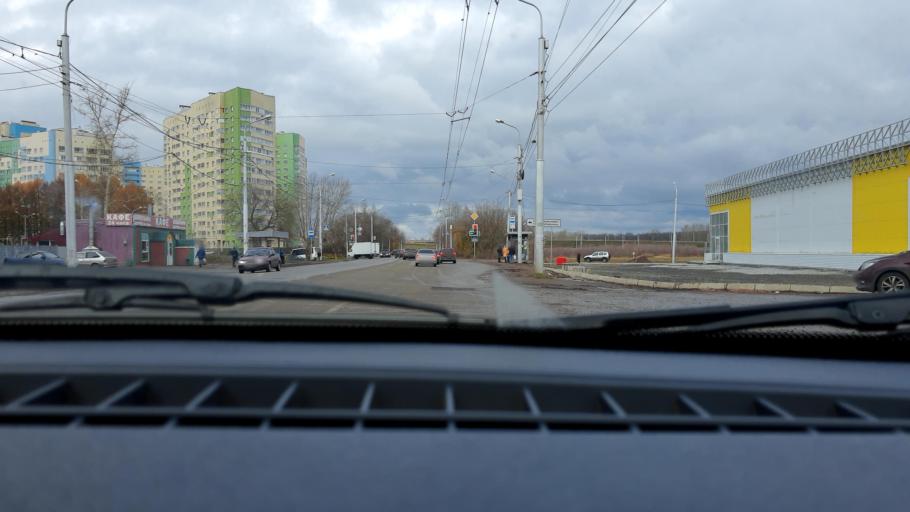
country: RU
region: Bashkortostan
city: Mikhaylovka
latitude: 54.7948
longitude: 55.8727
